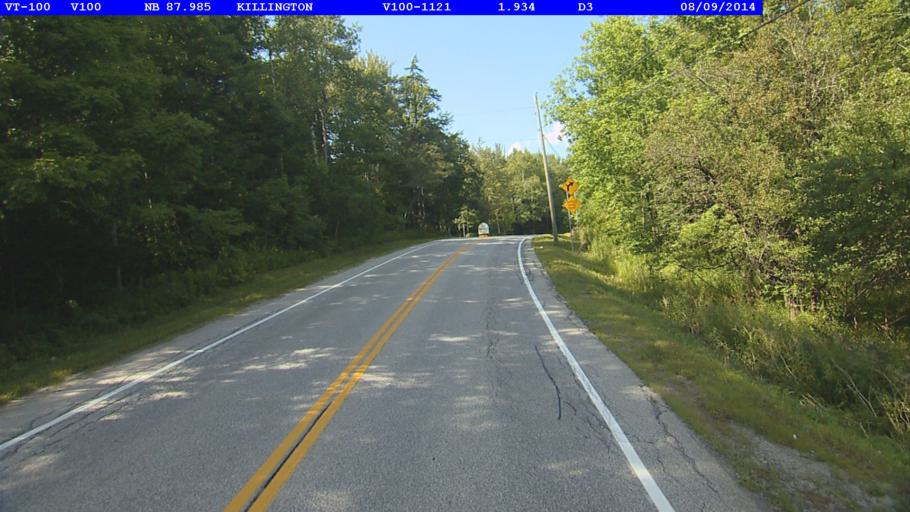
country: US
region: Vermont
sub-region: Rutland County
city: Rutland
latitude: 43.6930
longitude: -72.8141
